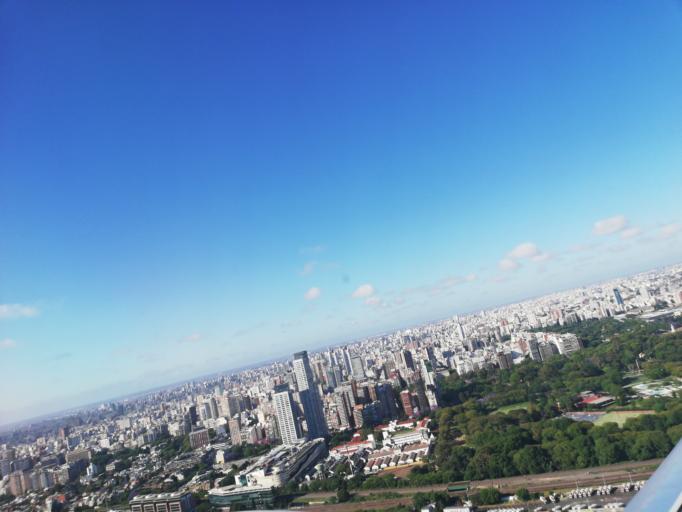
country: AR
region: Buenos Aires F.D.
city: Retiro
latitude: -34.5669
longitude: -58.4018
